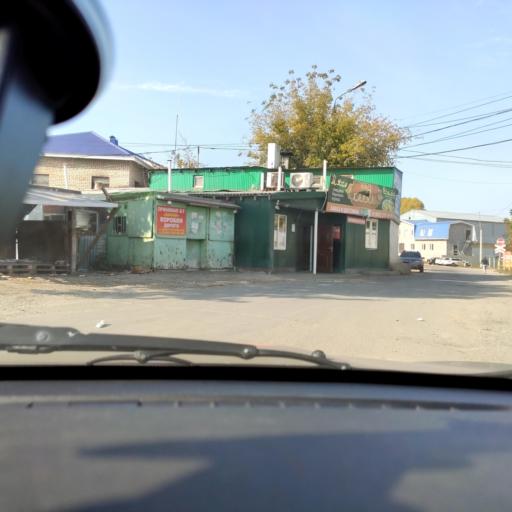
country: RU
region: Samara
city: Zhigulevsk
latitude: 53.5207
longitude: 49.4742
